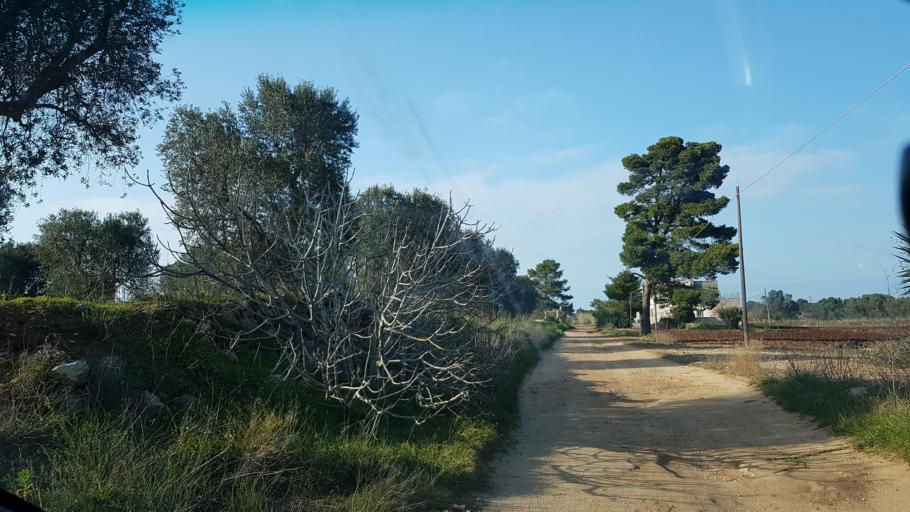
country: IT
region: Apulia
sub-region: Provincia di Brindisi
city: San Vito dei Normanni
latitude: 40.6789
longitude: 17.7892
